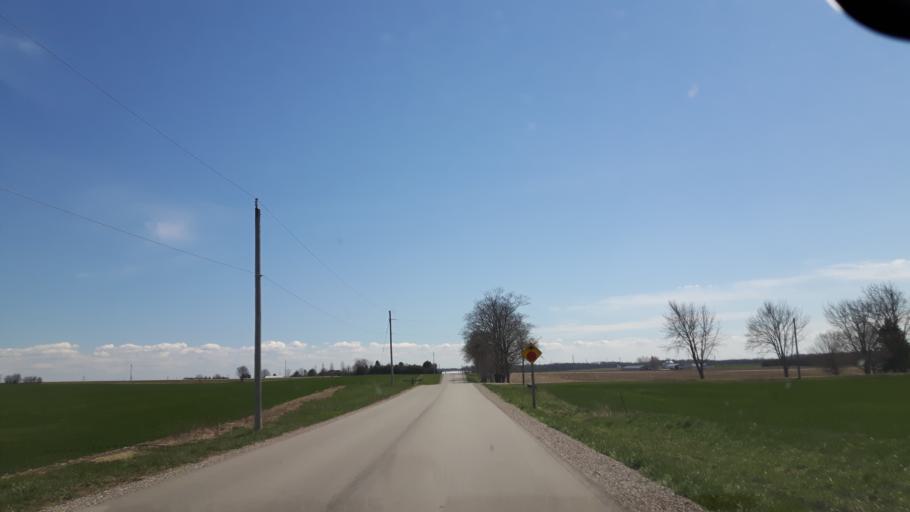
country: CA
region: Ontario
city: Bluewater
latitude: 43.5902
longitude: -81.6439
